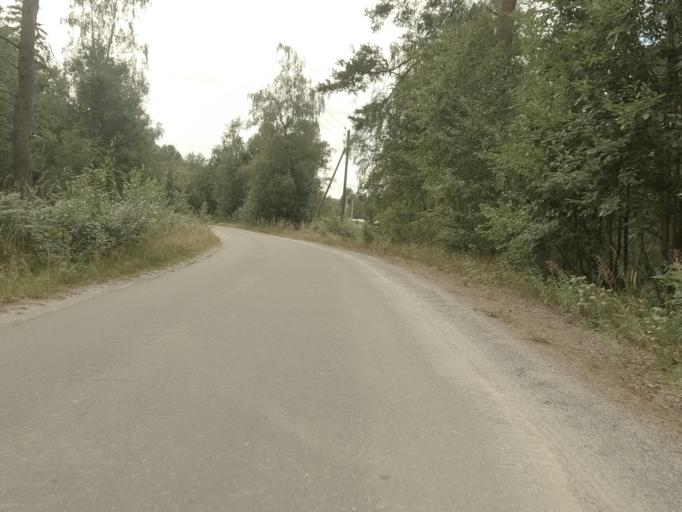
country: RU
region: Leningrad
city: Kamennogorsk
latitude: 60.9711
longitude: 29.1469
